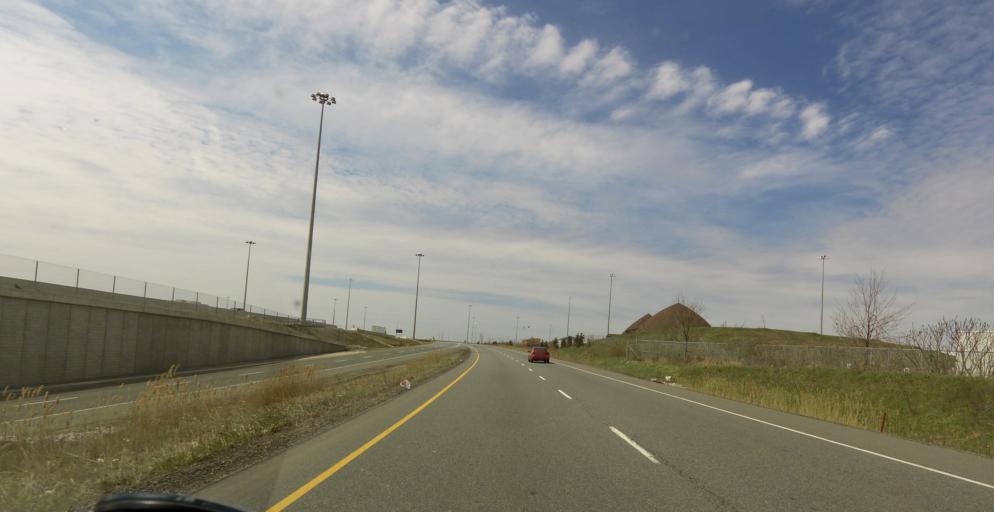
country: CA
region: Ontario
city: Mississauga
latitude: 43.6339
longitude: -79.6767
